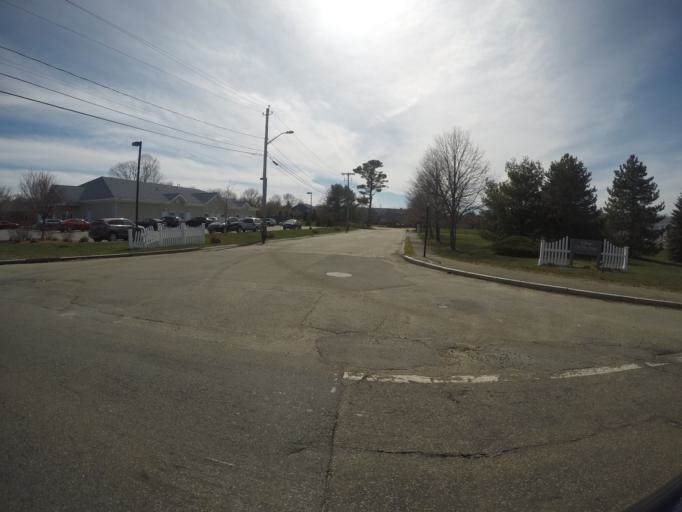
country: US
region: Massachusetts
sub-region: Bristol County
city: Easton
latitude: 42.0443
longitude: -71.0789
